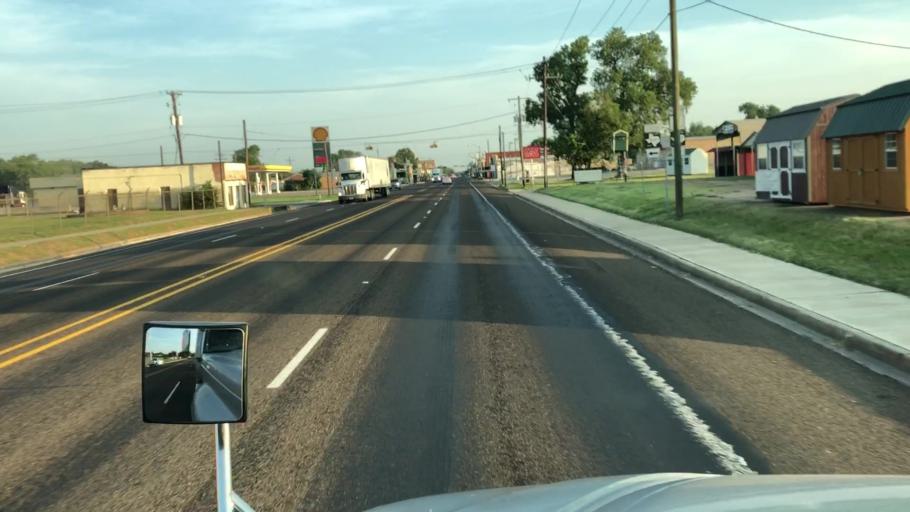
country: US
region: Texas
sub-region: Robertson County
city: Calvert
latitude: 30.9759
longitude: -96.6720
